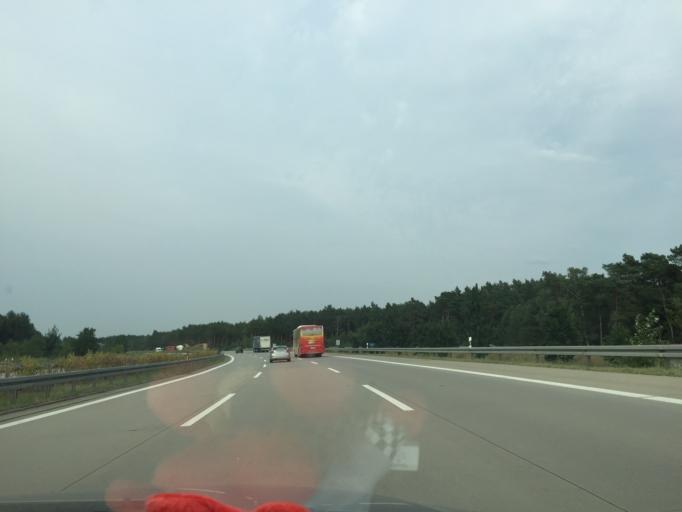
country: DE
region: Brandenburg
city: Erkner
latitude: 52.3268
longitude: 13.7488
